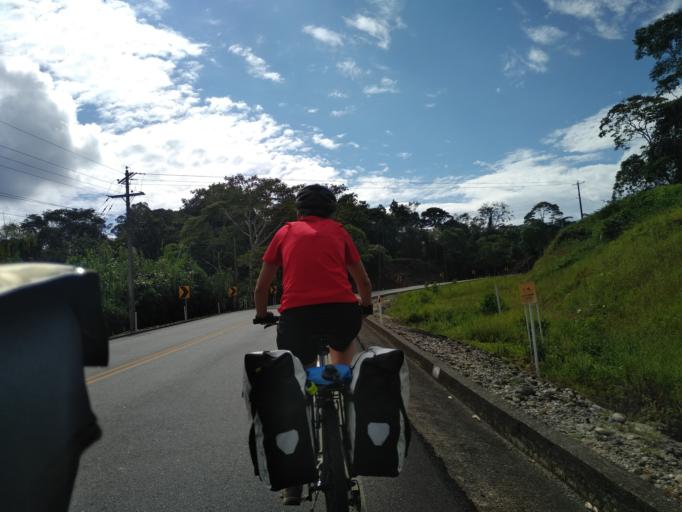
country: EC
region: Napo
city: Tena
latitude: -1.0876
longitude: -77.7894
